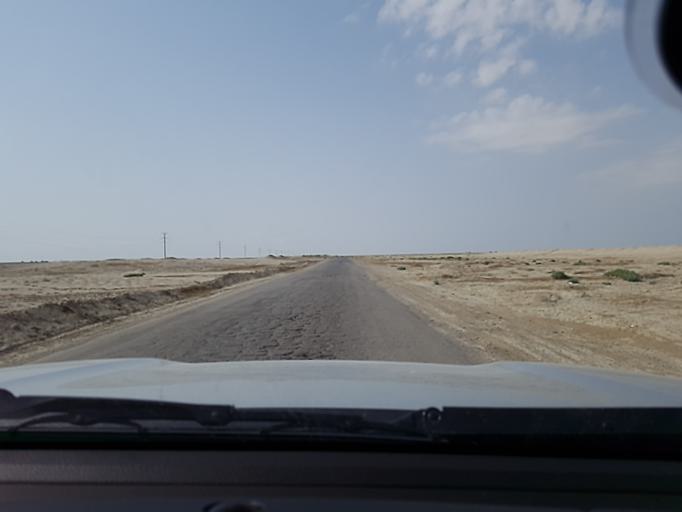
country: TM
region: Balkan
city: Gumdag
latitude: 39.0419
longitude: 54.5841
